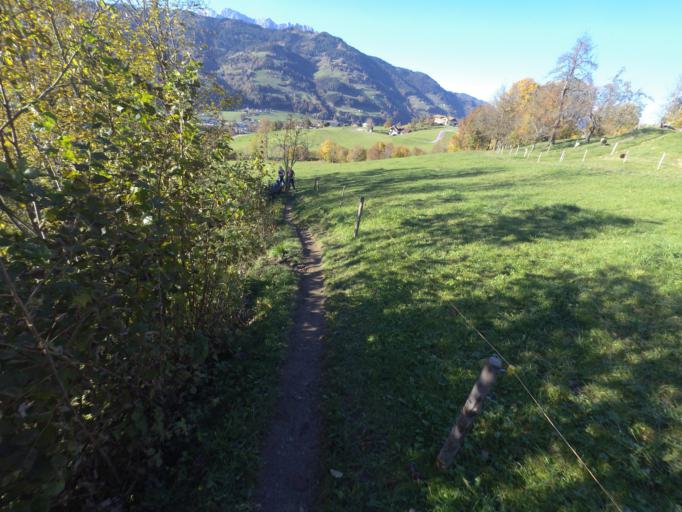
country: AT
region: Salzburg
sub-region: Politischer Bezirk Sankt Johann im Pongau
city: Sankt Johann im Pongau
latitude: 47.3472
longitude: 13.2186
